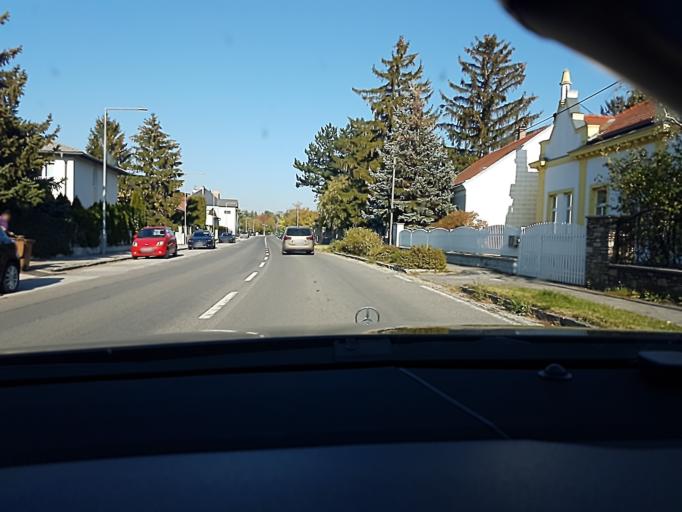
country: AT
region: Lower Austria
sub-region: Politischer Bezirk Wien-Umgebung
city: Lanzendorf
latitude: 48.1069
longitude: 16.4390
